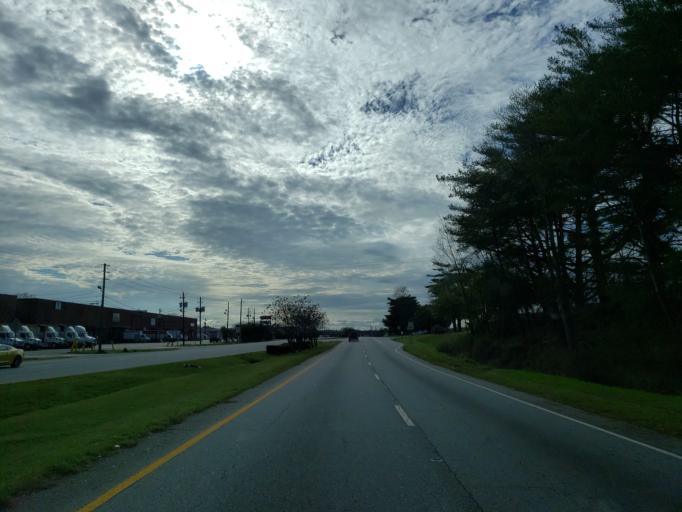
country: US
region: Georgia
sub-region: Clayton County
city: Forest Park
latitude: 33.6188
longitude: -84.3885
